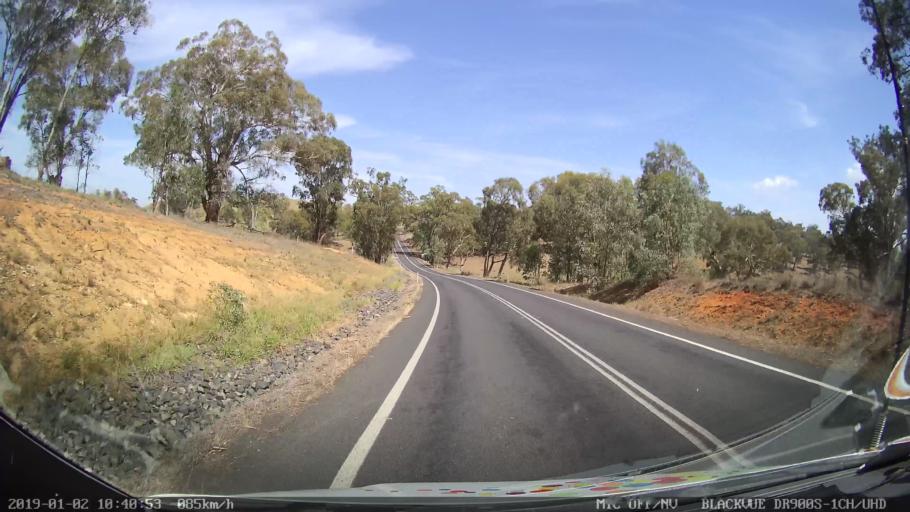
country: AU
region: New South Wales
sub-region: Cootamundra
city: Cootamundra
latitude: -34.7977
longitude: 148.3122
